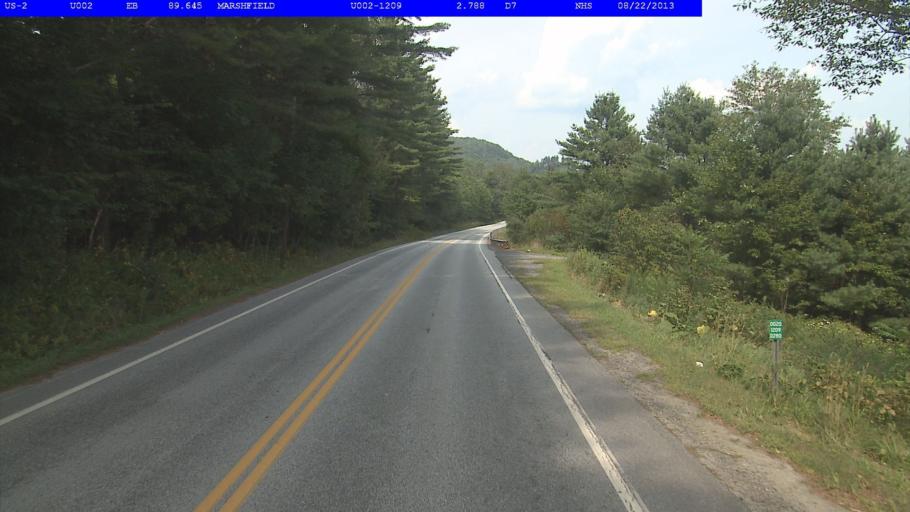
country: US
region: Vermont
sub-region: Washington County
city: Barre
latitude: 44.3107
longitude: -72.3972
